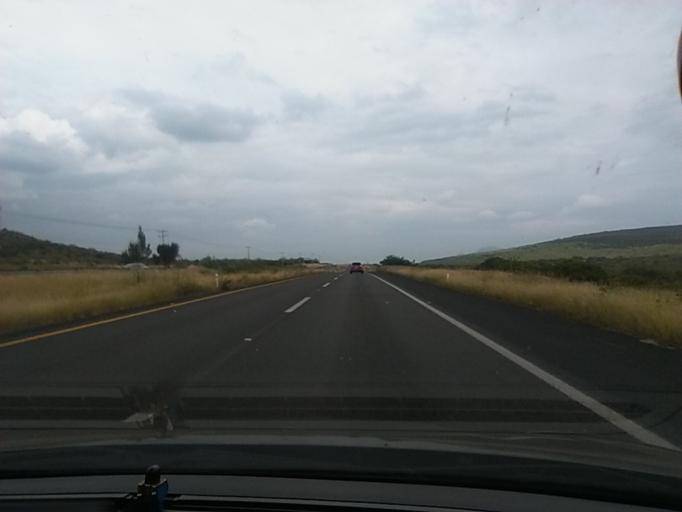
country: MX
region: Michoacan
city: Ecuandureo
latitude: 20.1742
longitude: -102.1720
